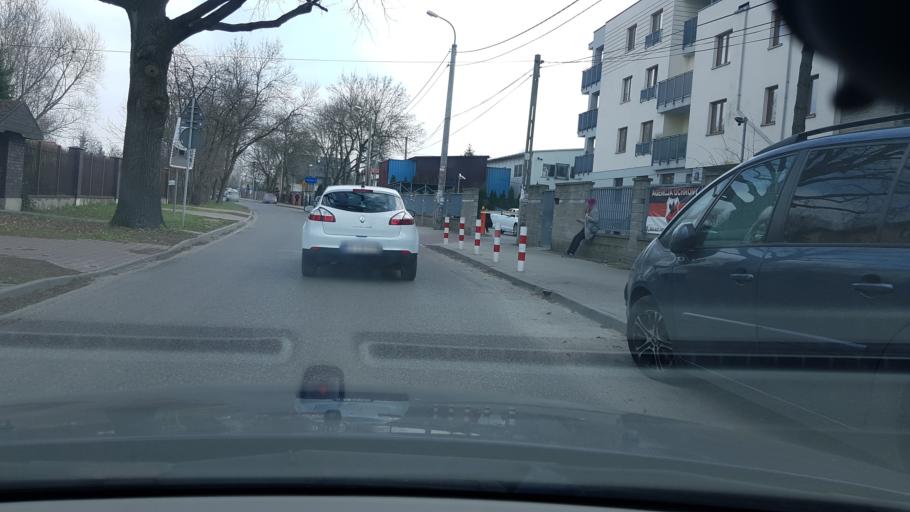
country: PL
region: Masovian Voivodeship
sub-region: Warszawa
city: Wesola
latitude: 52.2250
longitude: 21.2277
